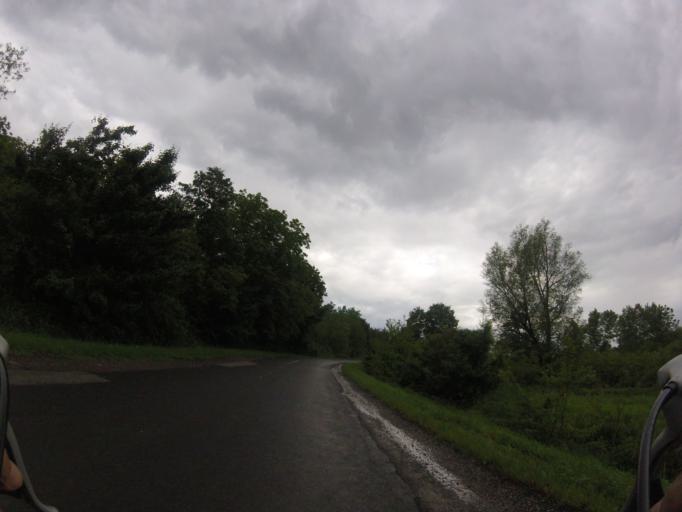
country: HU
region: Baranya
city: Pellerd
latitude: 45.9619
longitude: 18.2026
